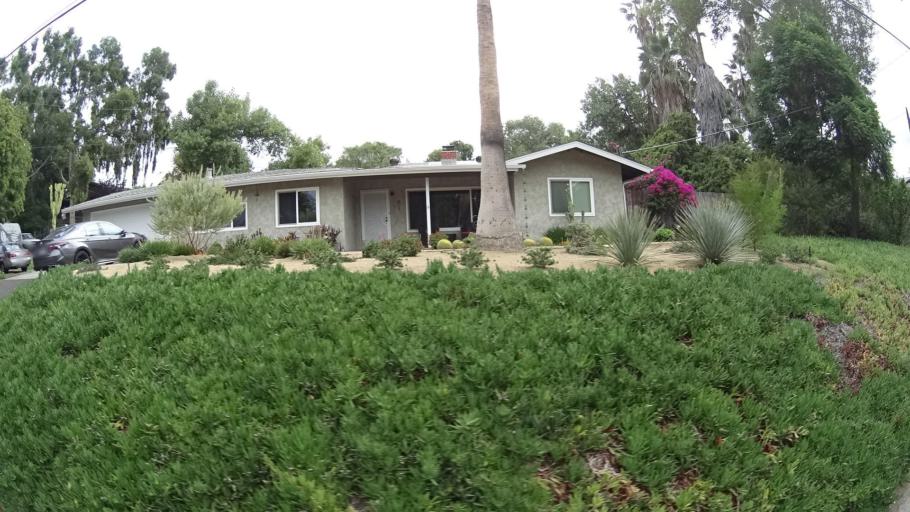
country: US
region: California
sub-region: San Diego County
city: Spring Valley
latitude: 32.7563
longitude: -116.9989
